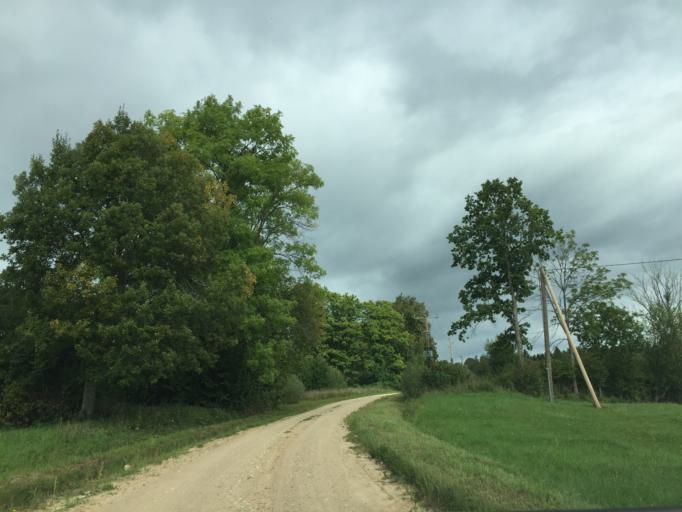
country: LV
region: Pargaujas
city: Stalbe
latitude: 57.5127
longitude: 24.9155
